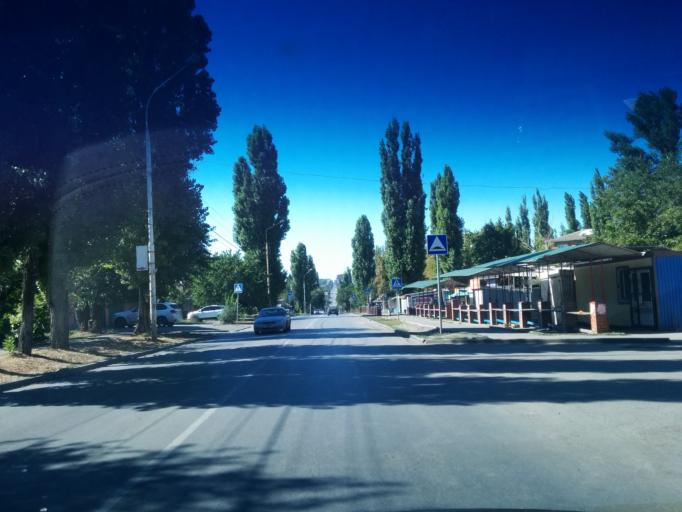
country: RU
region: Rostov
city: Shakhty
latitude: 47.6941
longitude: 40.2460
